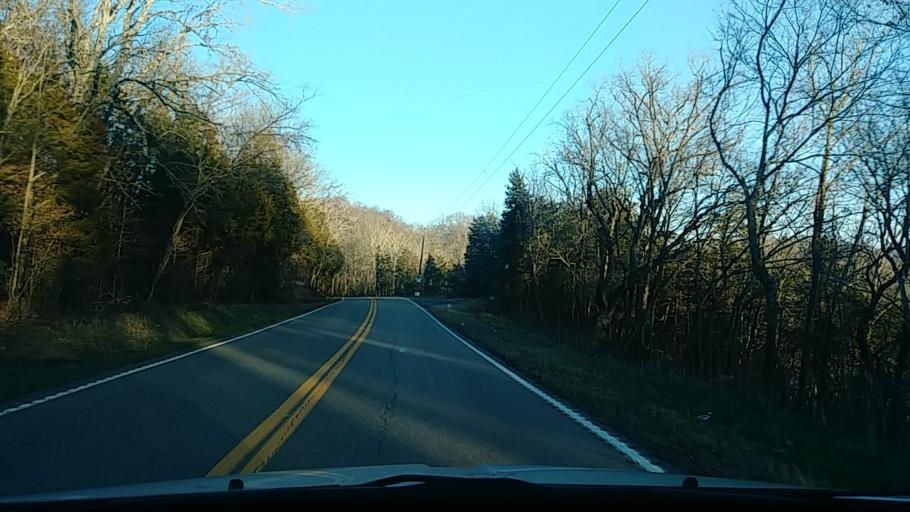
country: US
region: Tennessee
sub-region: Jefferson County
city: White Pine
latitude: 36.1237
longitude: -83.1207
